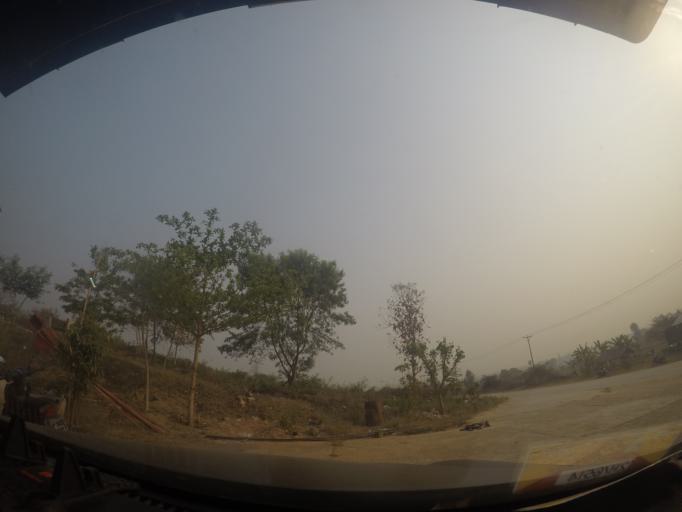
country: MM
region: Mandalay
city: Nay Pyi Taw
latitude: 19.8807
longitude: 96.0252
